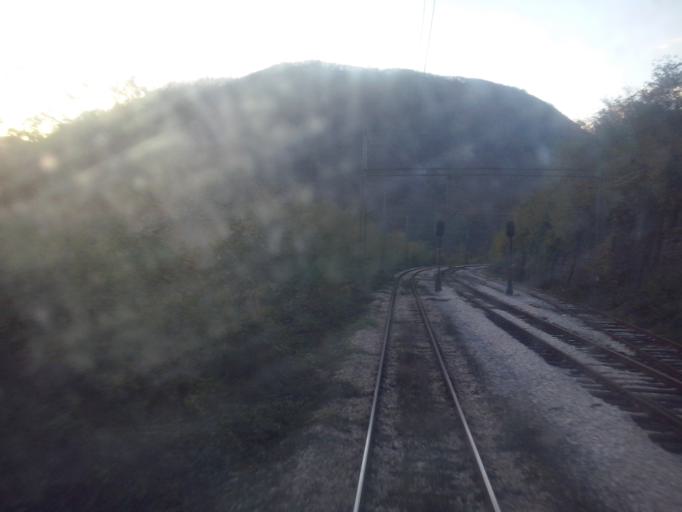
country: RS
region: Central Serbia
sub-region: Kolubarski Okrug
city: Valjevo
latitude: 44.1550
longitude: 19.8899
